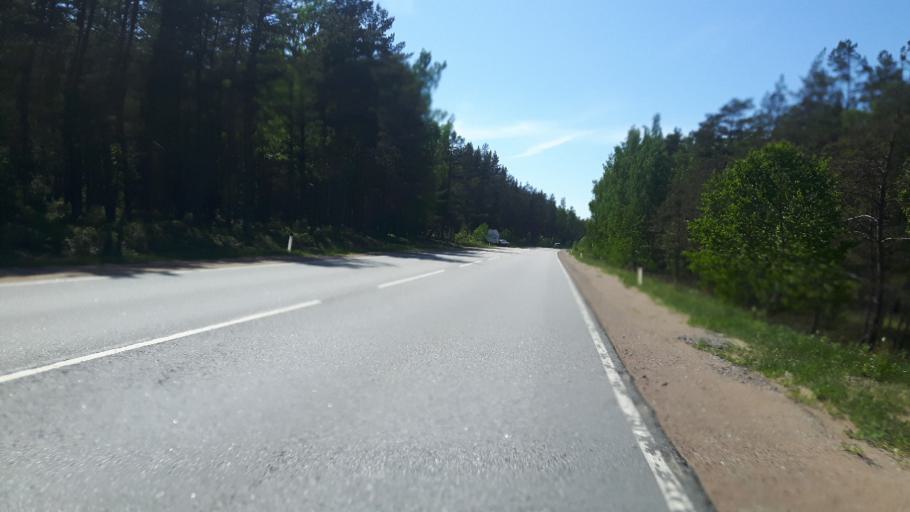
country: RU
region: Leningrad
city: Sista-Palkino
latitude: 59.7667
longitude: 28.7420
